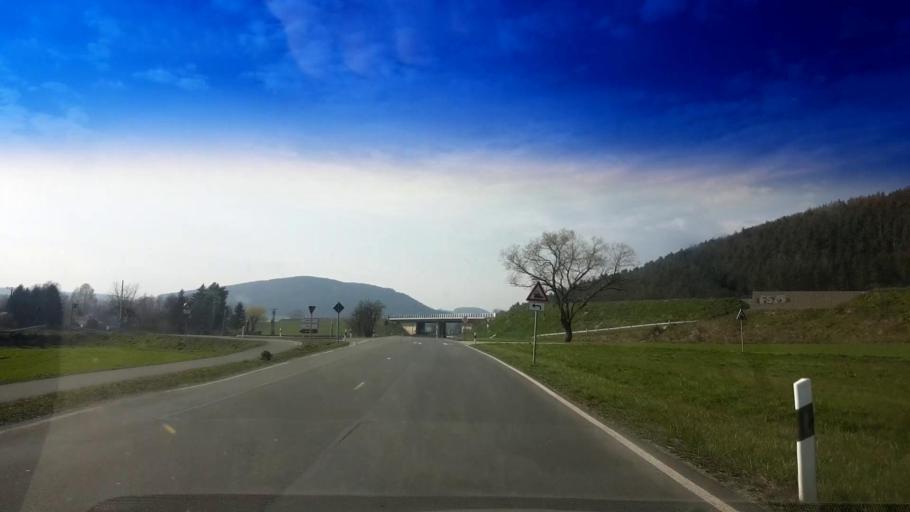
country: DE
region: Bavaria
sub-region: Upper Franconia
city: Harsdorf
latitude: 50.0315
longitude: 11.5622
